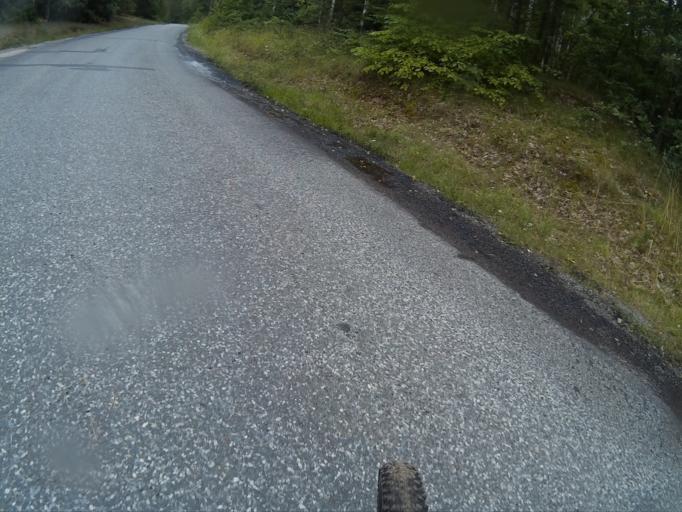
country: PL
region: Kujawsko-Pomorskie
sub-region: Powiat tucholski
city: Tuchola
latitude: 53.5659
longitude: 17.9034
